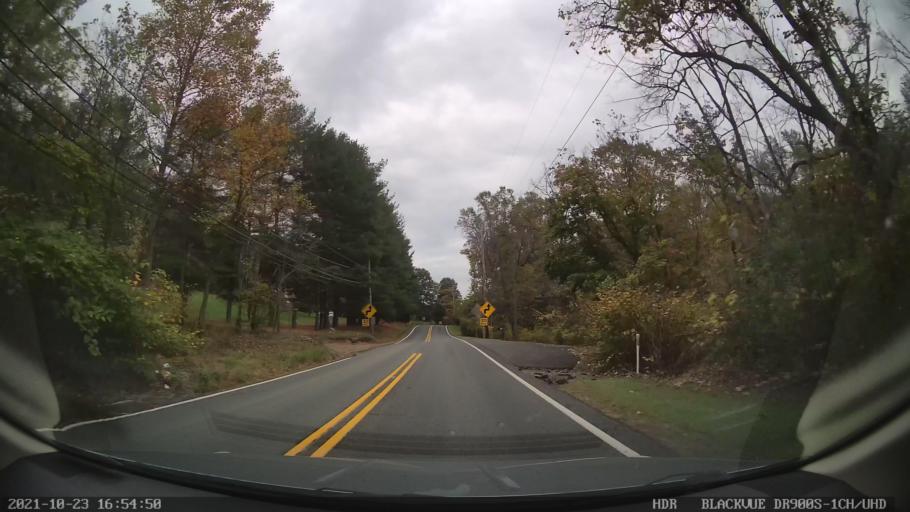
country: US
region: Pennsylvania
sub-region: Berks County
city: Red Lion
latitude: 40.4588
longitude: -75.5699
